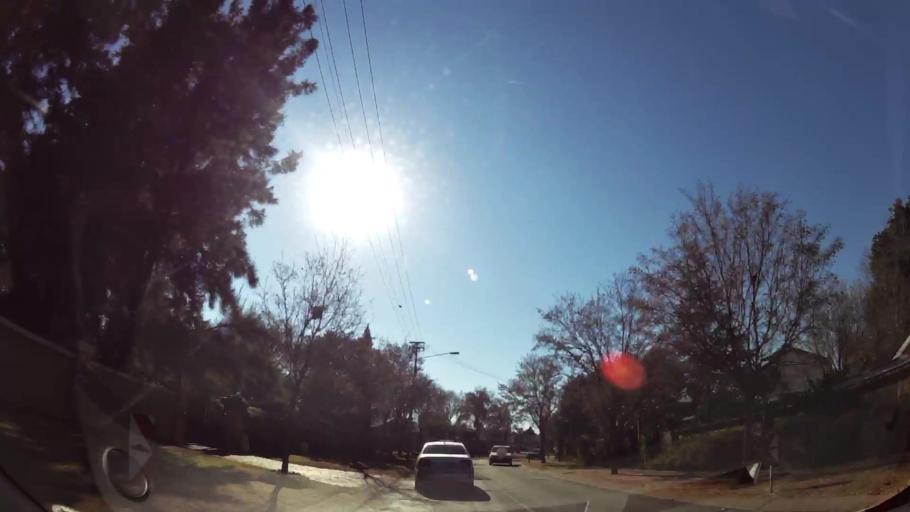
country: ZA
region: Gauteng
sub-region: City of Tshwane Metropolitan Municipality
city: Centurion
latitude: -25.8549
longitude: 28.2078
